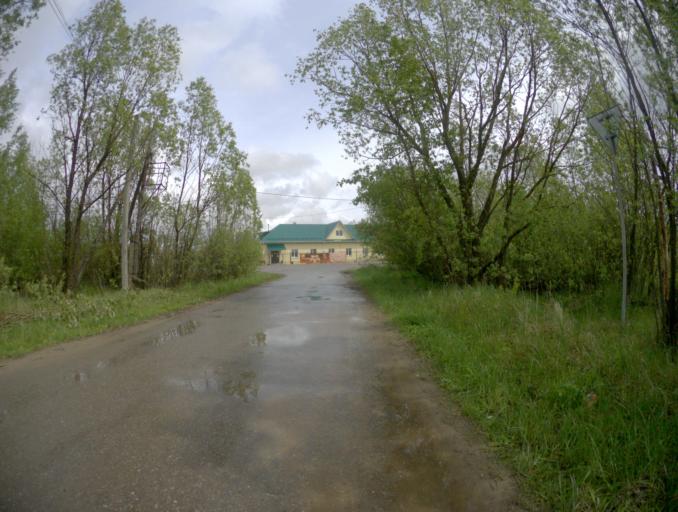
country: RU
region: Vladimir
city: Zolotkovo
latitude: 55.3326
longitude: 41.0239
